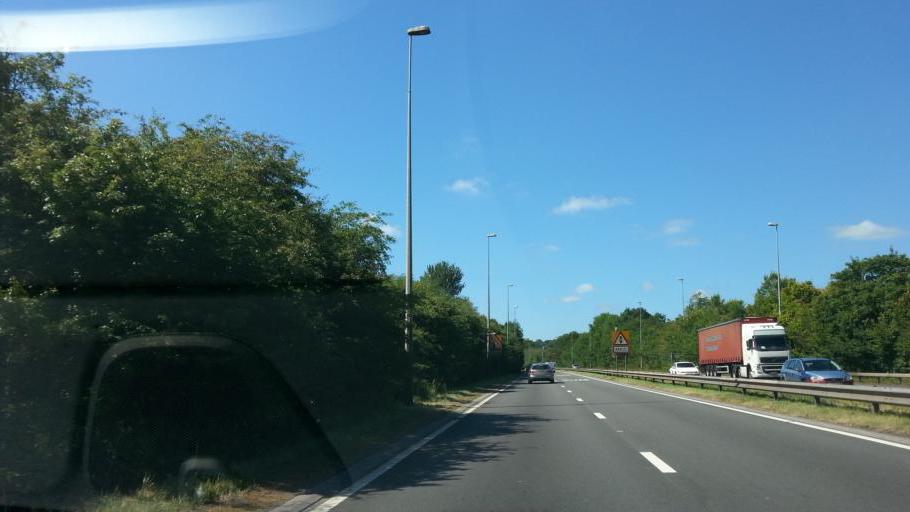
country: GB
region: Wales
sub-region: Monmouthshire
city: Monmouth
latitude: 51.8154
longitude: -2.7059
